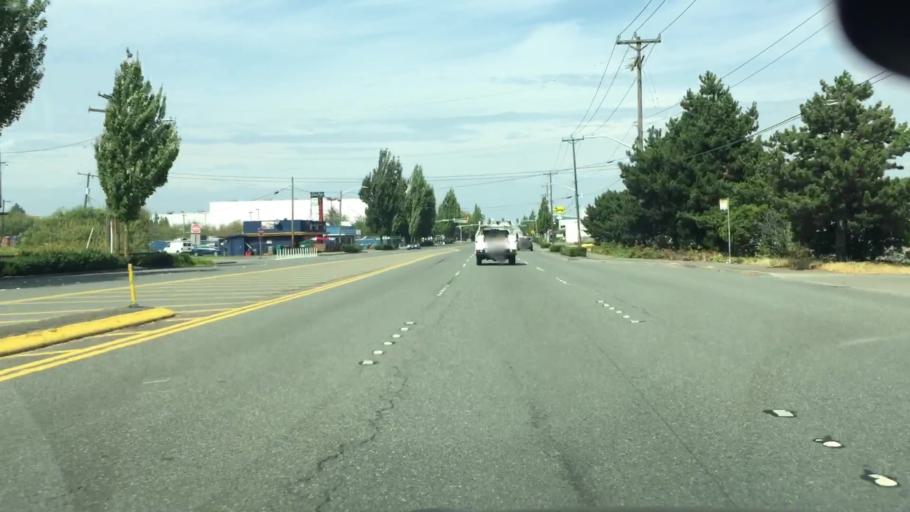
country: US
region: Washington
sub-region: King County
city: Riverton
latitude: 47.5096
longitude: -122.2920
